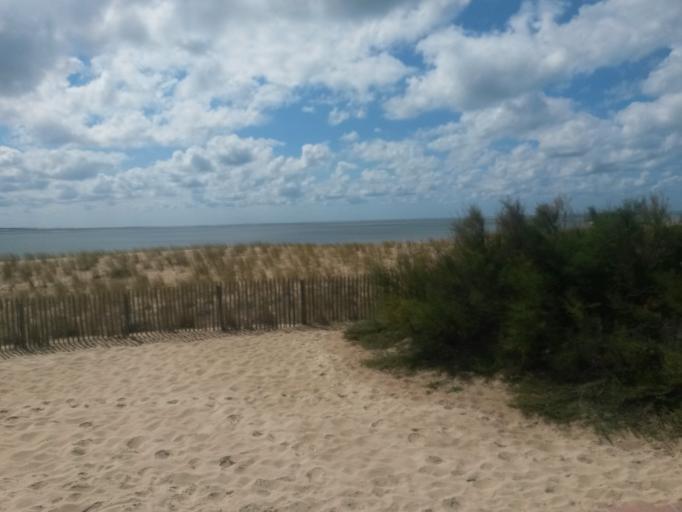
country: FR
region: Aquitaine
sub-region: Departement de la Gironde
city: Arcachon
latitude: 44.6222
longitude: -1.2473
